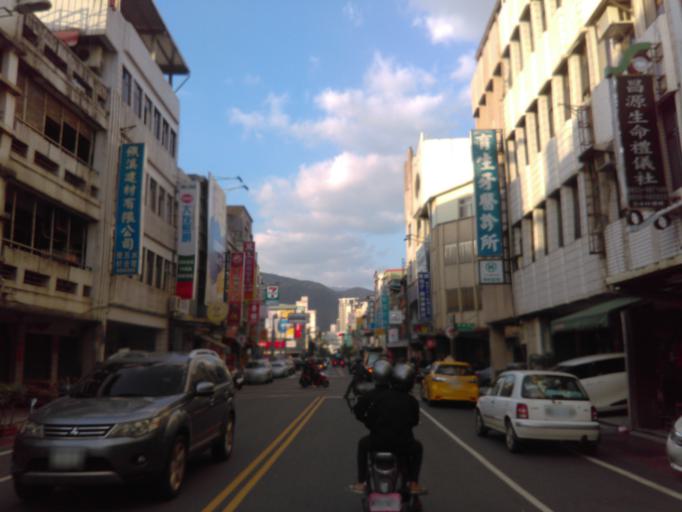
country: TW
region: Taiwan
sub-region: Yilan
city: Yilan
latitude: 24.8201
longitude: 121.7707
